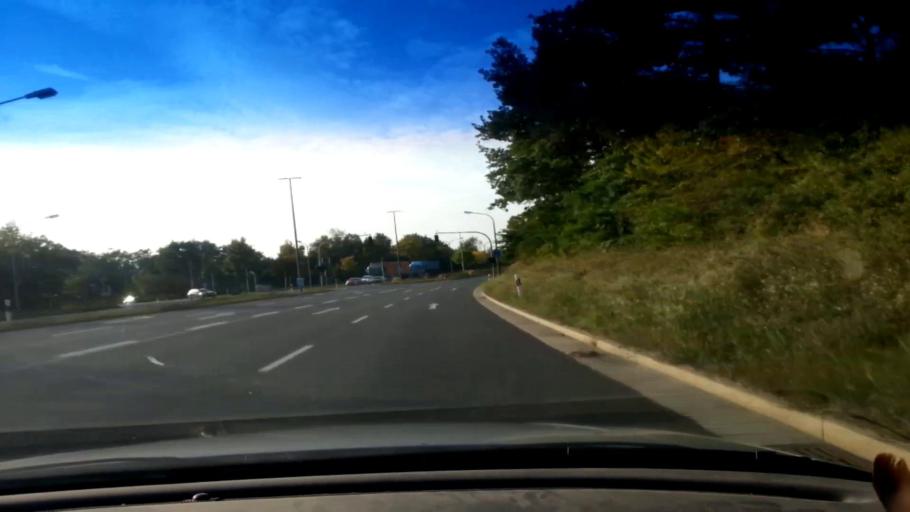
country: DE
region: Bavaria
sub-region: Upper Franconia
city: Bamberg
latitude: 49.8798
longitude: 10.9256
